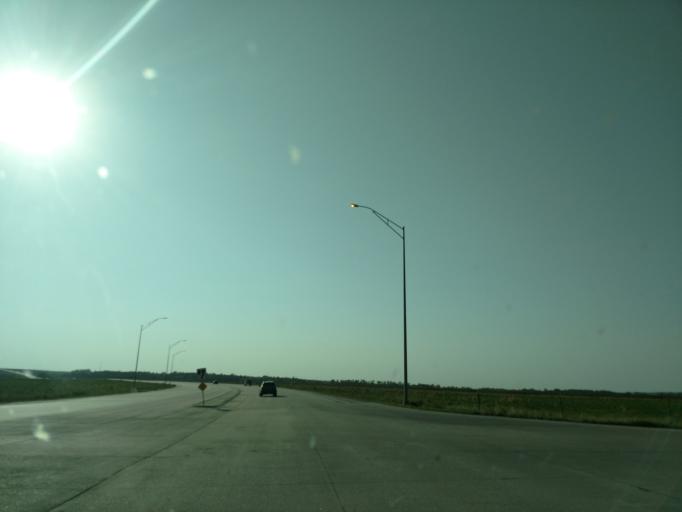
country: US
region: Nebraska
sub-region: Sarpy County
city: Offutt Air Force Base
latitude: 41.0768
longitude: -95.8910
